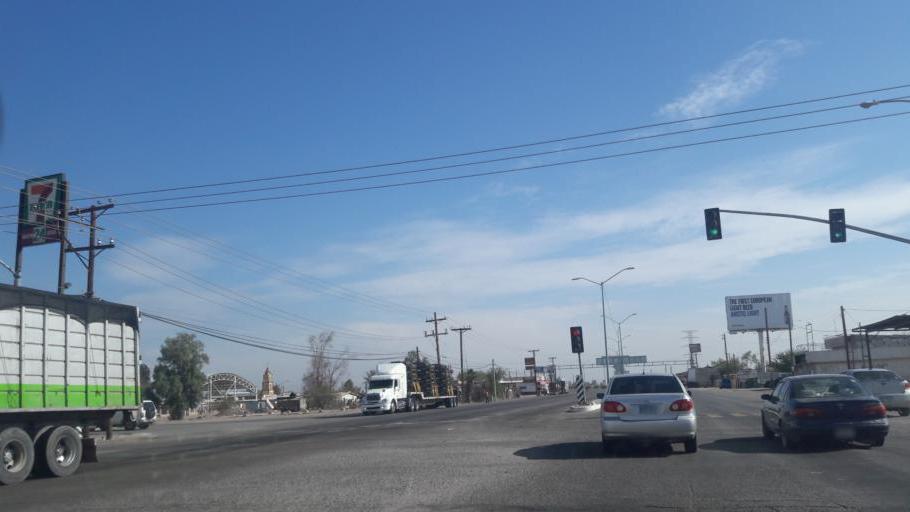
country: MX
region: Baja California
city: Progreso
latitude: 32.5817
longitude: -115.5845
